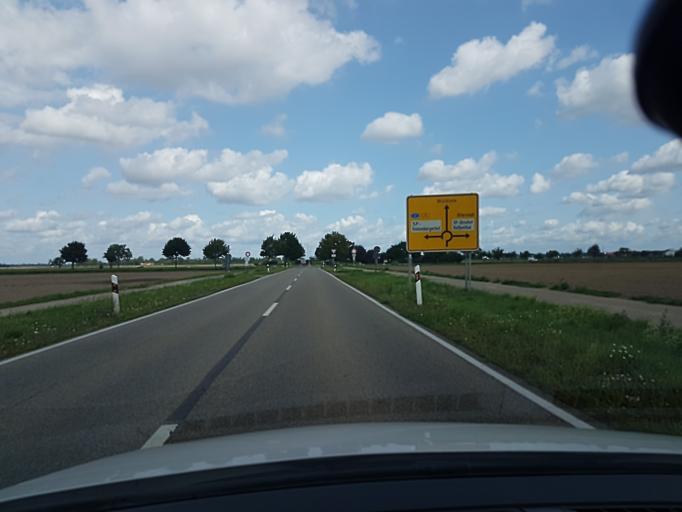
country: DE
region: Rheinland-Pfalz
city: Otterstadt
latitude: 49.3626
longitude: 8.4374
